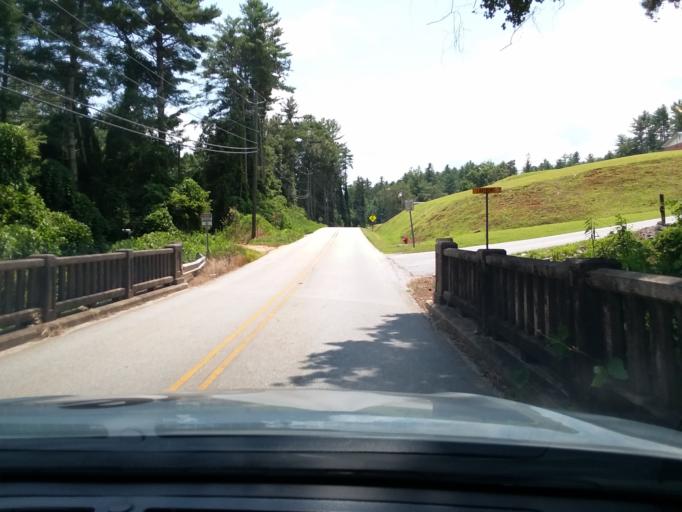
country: US
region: Georgia
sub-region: Rabun County
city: Clayton
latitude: 34.7916
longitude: -83.4160
